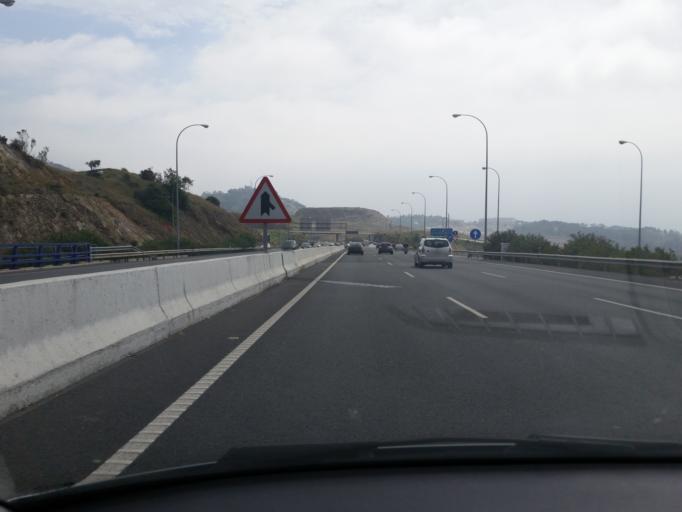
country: ES
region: Andalusia
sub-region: Provincia de Malaga
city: Malaga
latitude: 36.7429
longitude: -4.4049
